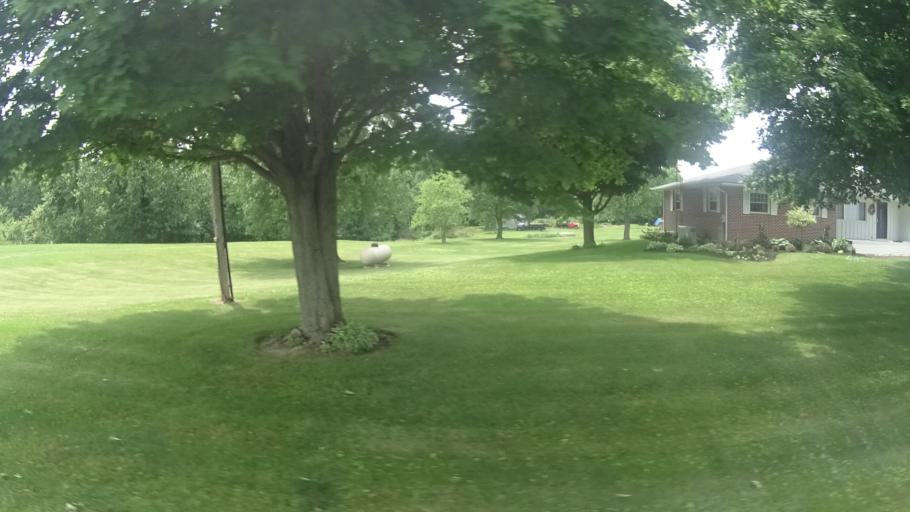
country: US
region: Ohio
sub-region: Erie County
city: Milan
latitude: 41.2986
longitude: -82.6516
